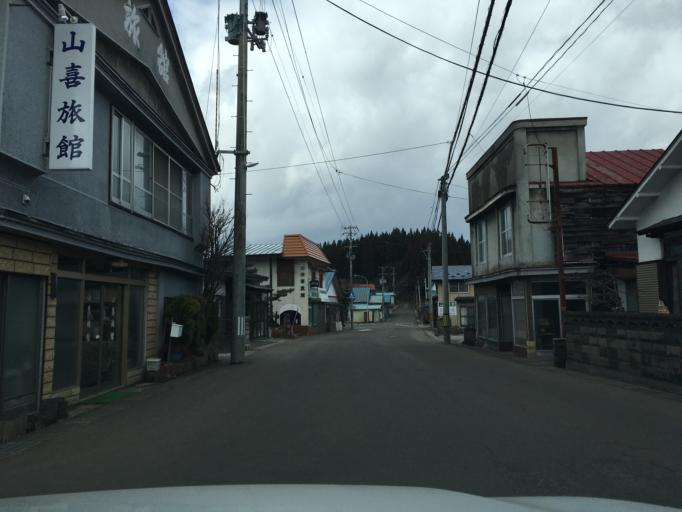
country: JP
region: Akita
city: Takanosu
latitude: 40.1616
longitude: 140.3289
